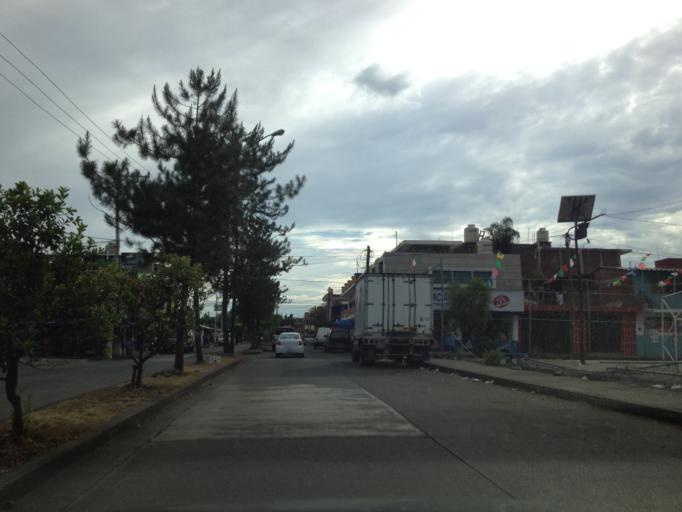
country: MX
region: Michoacan
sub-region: Uruapan
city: Uruapan
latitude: 19.4107
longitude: -102.0384
